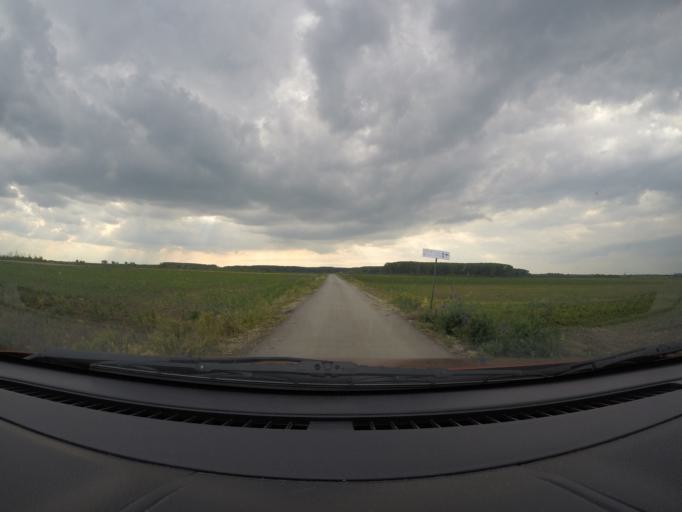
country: RS
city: Uzdin
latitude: 45.2033
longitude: 20.5992
